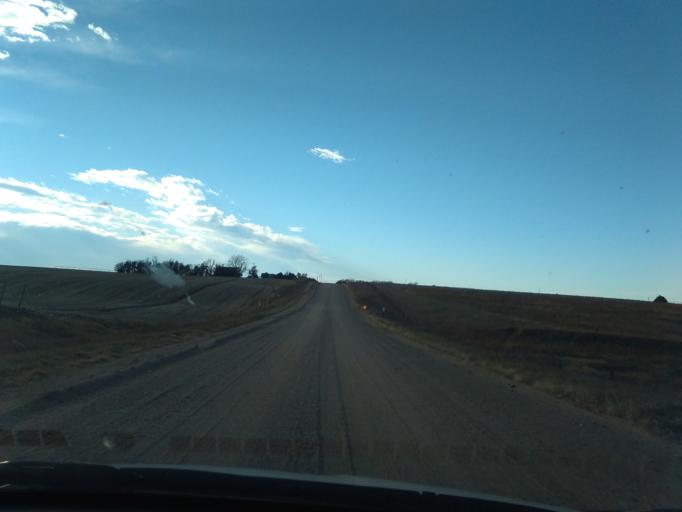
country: US
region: Nebraska
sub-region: Kearney County
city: Minden
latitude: 40.3649
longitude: -98.9069
